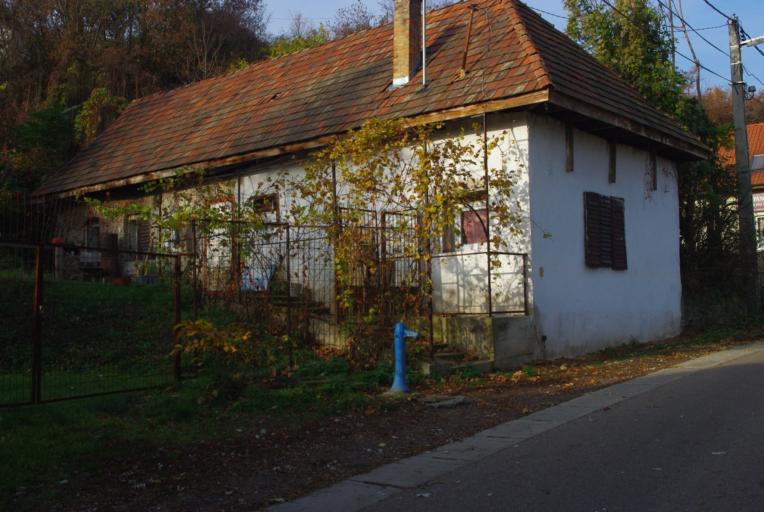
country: HU
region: Borsod-Abauj-Zemplen
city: Satoraljaujhely
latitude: 48.3966
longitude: 21.6487
